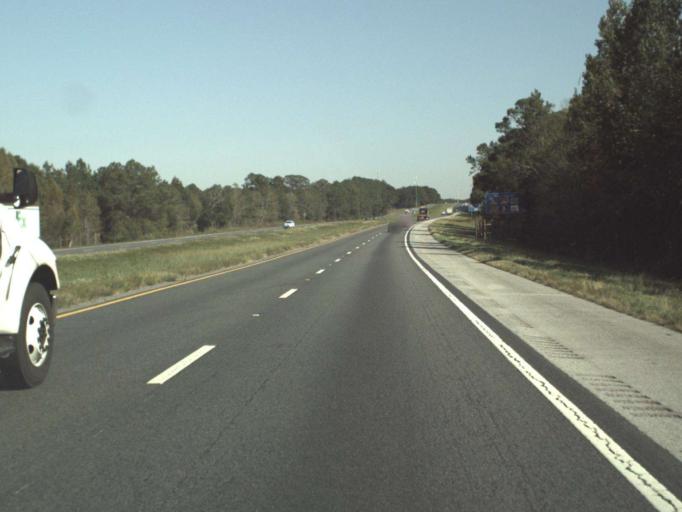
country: US
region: Florida
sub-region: Washington County
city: Chipley
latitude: 30.7500
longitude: -85.5643
